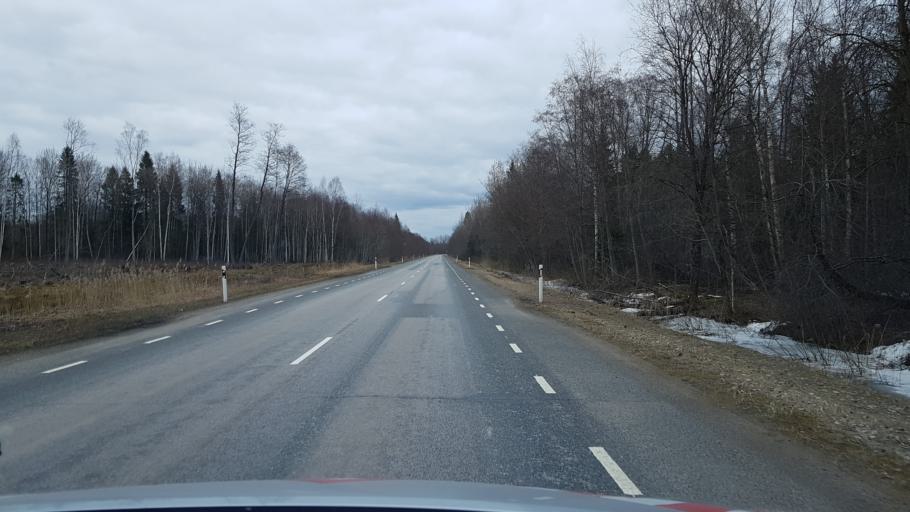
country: EE
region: Ida-Virumaa
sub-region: Narva linn
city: Narva
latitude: 59.3528
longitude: 28.0802
